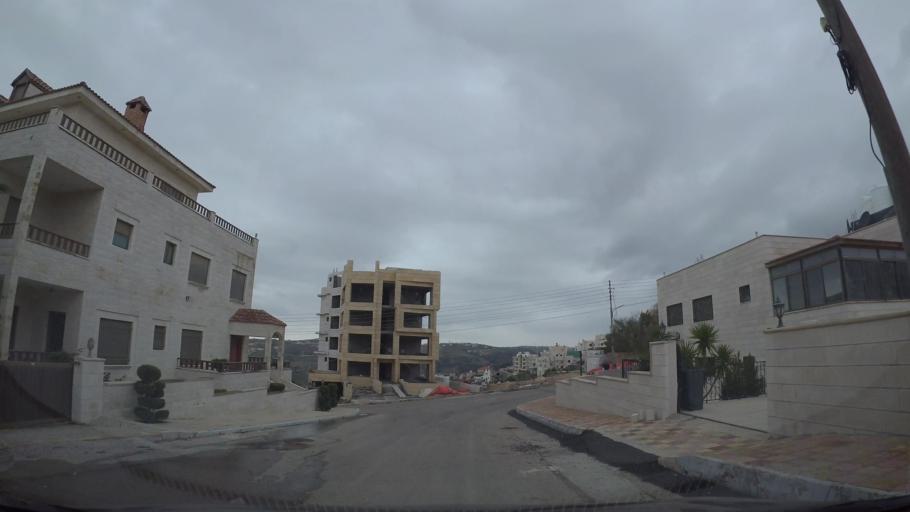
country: JO
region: Amman
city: Wadi as Sir
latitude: 31.9619
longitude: 35.8227
